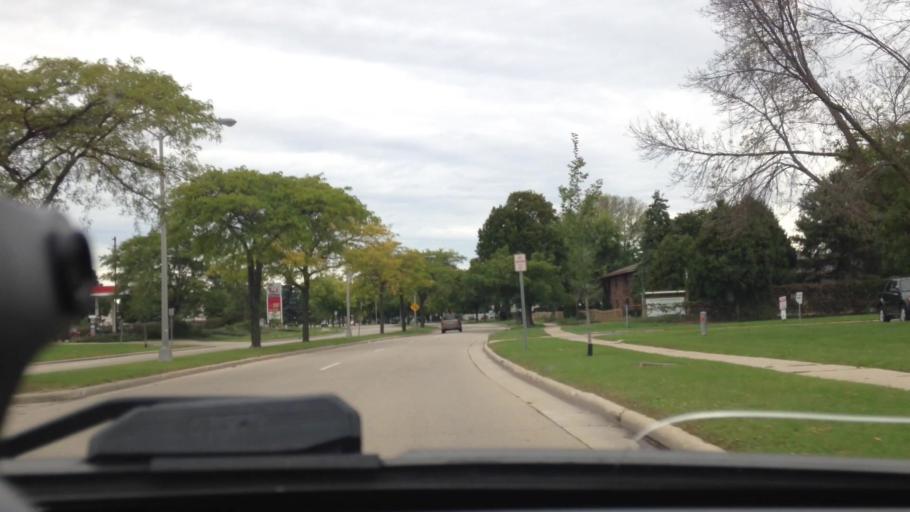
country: US
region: Wisconsin
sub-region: Fond du Lac County
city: North Fond du Lac
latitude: 43.7879
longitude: -88.4730
